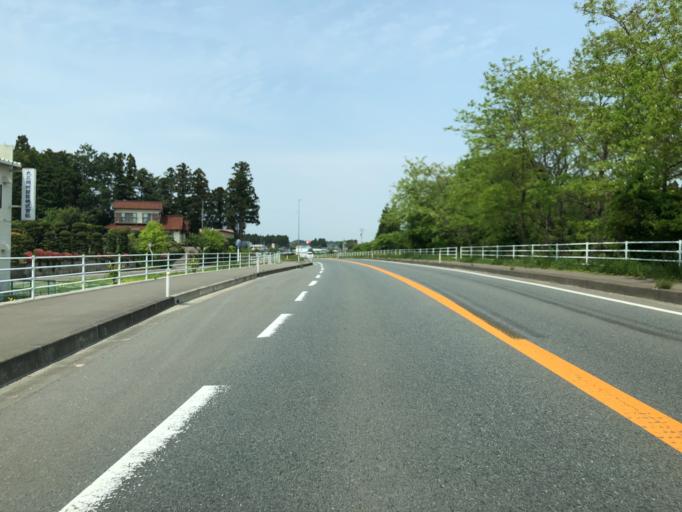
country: JP
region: Miyagi
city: Marumori
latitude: 37.8640
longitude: 140.9208
